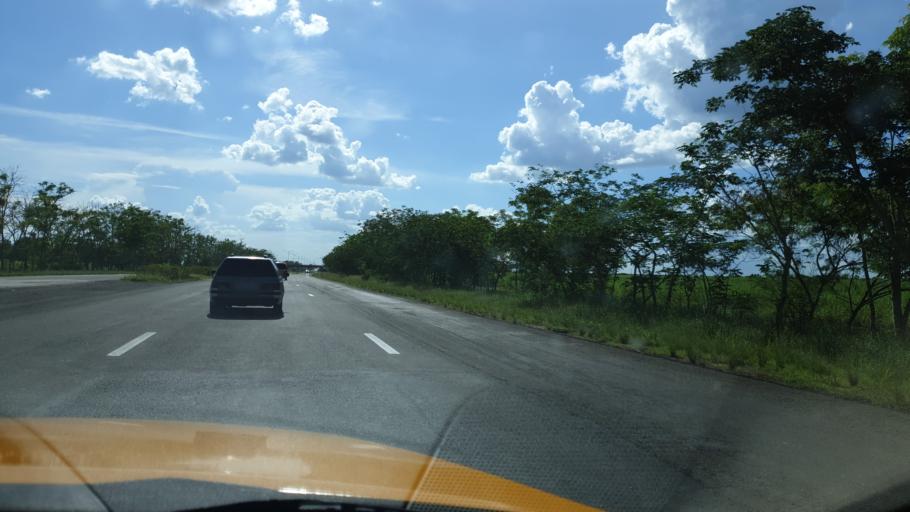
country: CU
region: Cienfuegos
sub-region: Municipio de Aguada de Pasajeros
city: Aguada de Pasajeros
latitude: 22.4024
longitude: -80.8563
